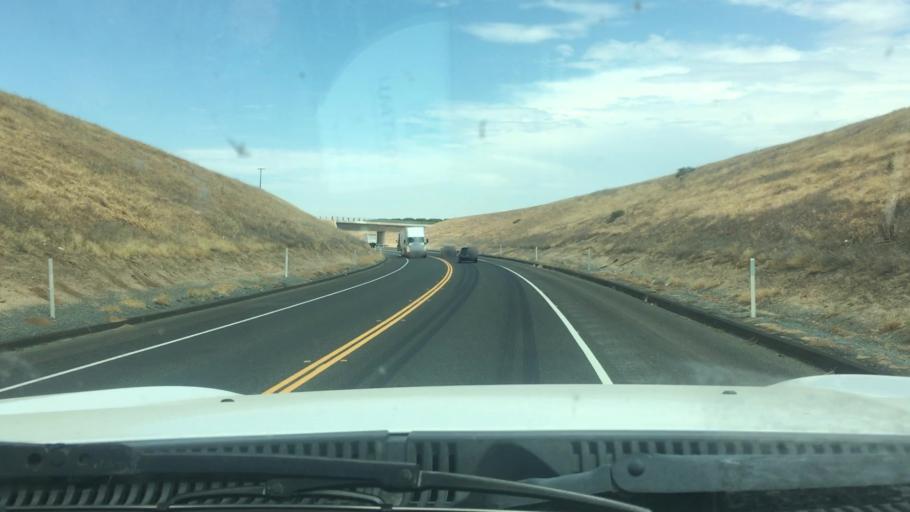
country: US
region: California
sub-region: Tulare County
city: Richgrove
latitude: 35.8667
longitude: -119.0521
